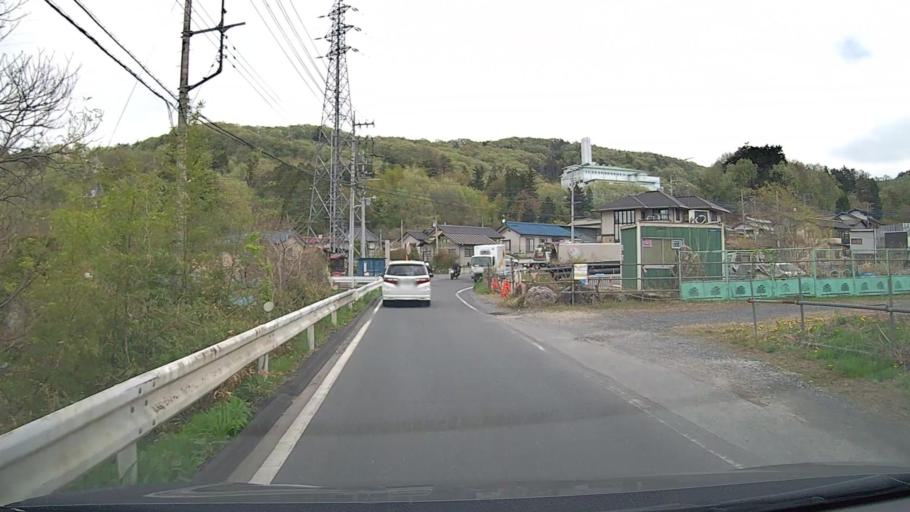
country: JP
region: Saitama
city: Chichibu
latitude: 36.0279
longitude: 139.1213
